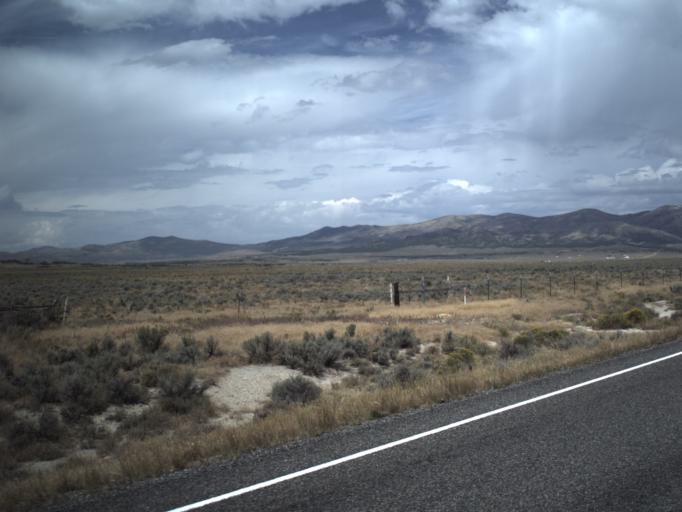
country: US
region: Idaho
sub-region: Cassia County
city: Burley
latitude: 41.7424
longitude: -113.5188
